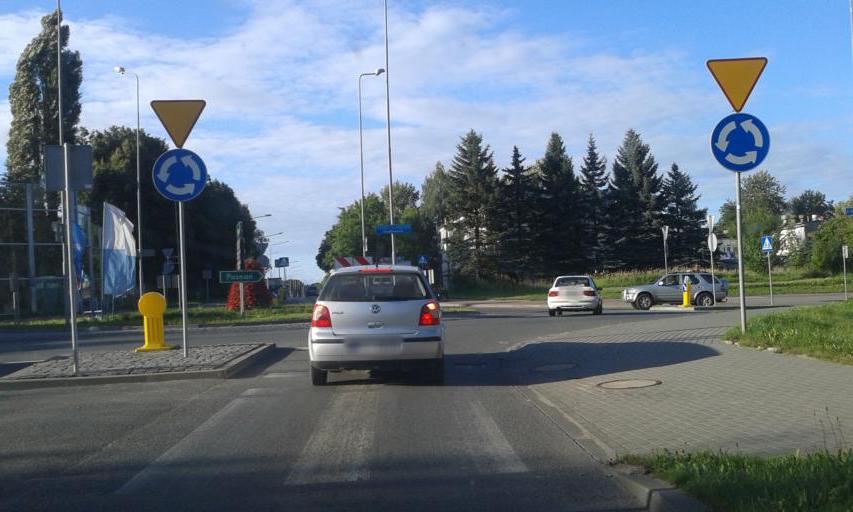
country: PL
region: West Pomeranian Voivodeship
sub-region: Koszalin
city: Koszalin
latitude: 54.1749
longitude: 16.1846
